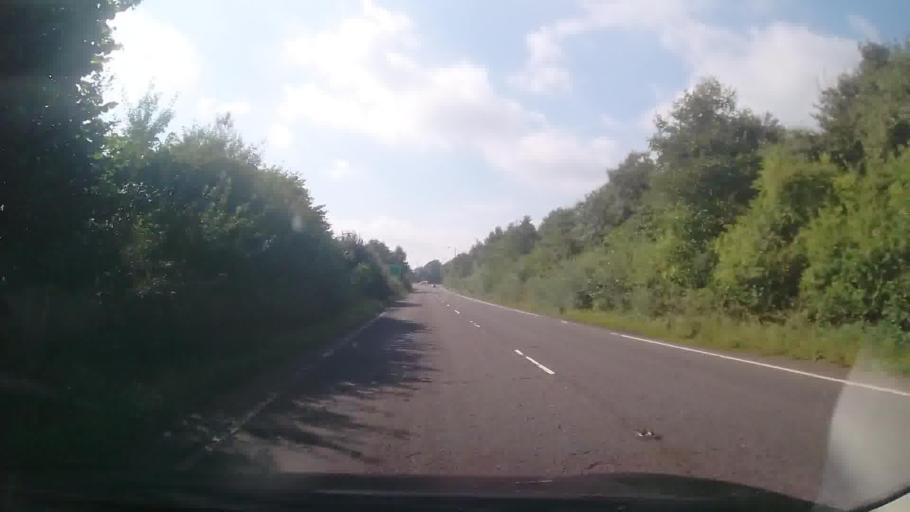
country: GB
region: England
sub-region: Shropshire
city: Whitchurch
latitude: 52.9798
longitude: -2.7007
